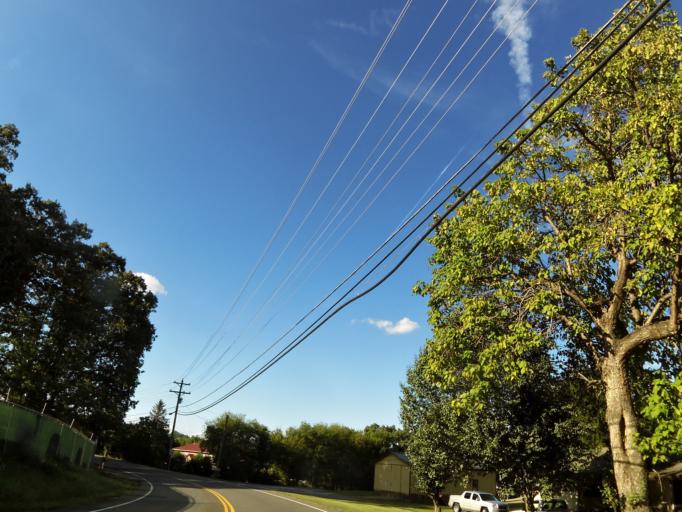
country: US
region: Tennessee
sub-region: Blount County
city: Alcoa
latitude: 35.8345
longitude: -83.9787
